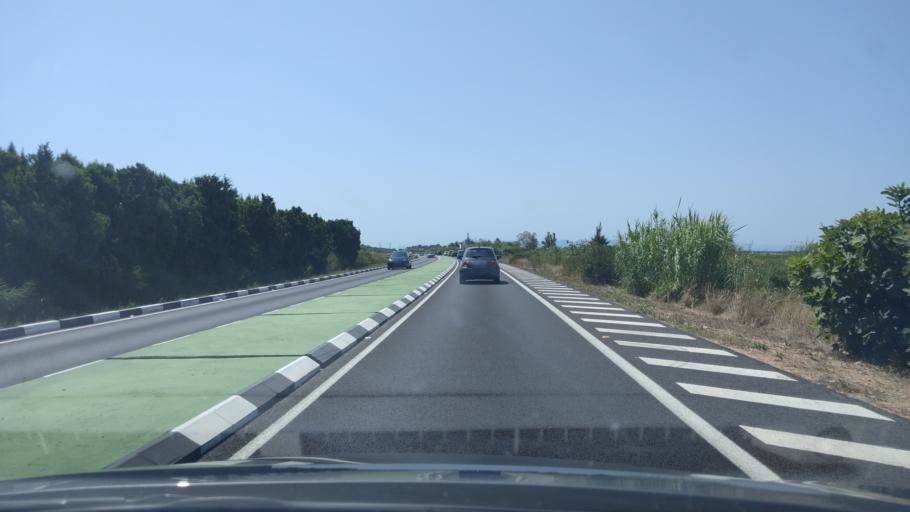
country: ES
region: Valencia
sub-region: Provincia de Valencia
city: Alfafar
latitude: 39.3817
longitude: -0.3343
